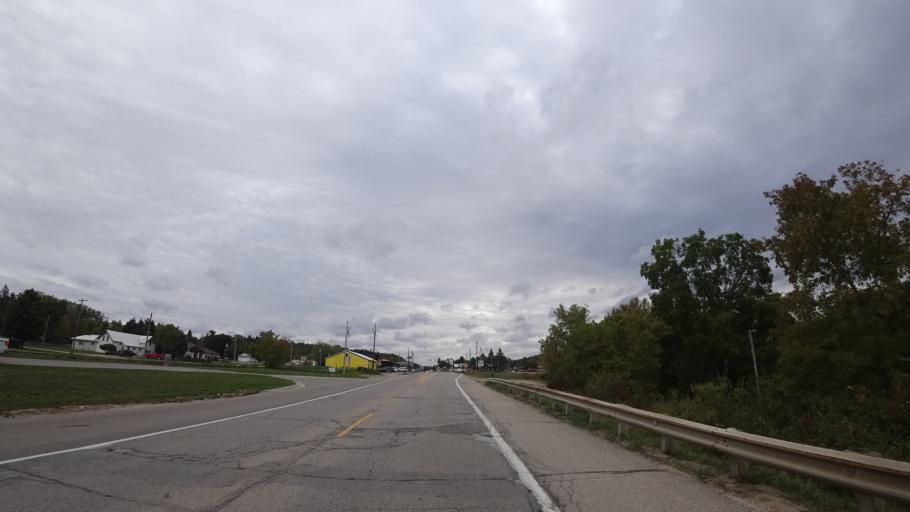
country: US
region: Michigan
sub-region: Charlevoix County
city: Boyne City
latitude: 45.1698
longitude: -84.9159
